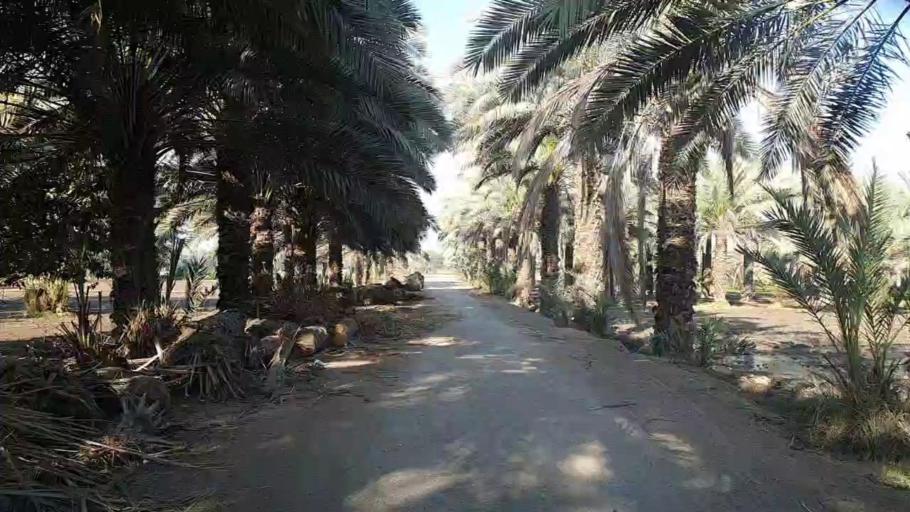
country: PK
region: Sindh
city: Ranipur
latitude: 27.2575
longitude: 68.5528
